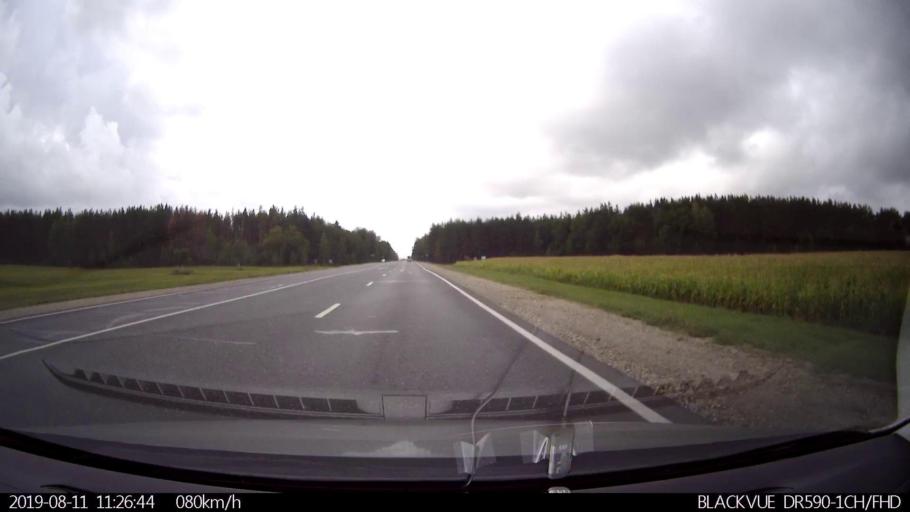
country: RU
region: Ulyanovsk
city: Krasnyy Gulyay
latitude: 54.1017
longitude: 48.2341
